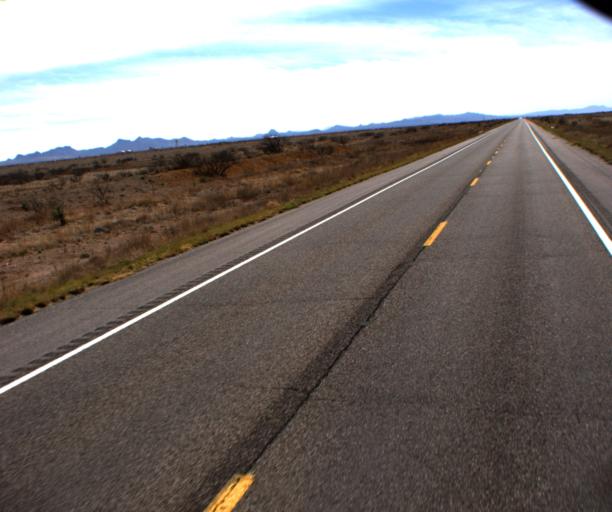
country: US
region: Arizona
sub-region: Cochise County
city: Pirtleville
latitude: 31.4806
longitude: -109.6245
